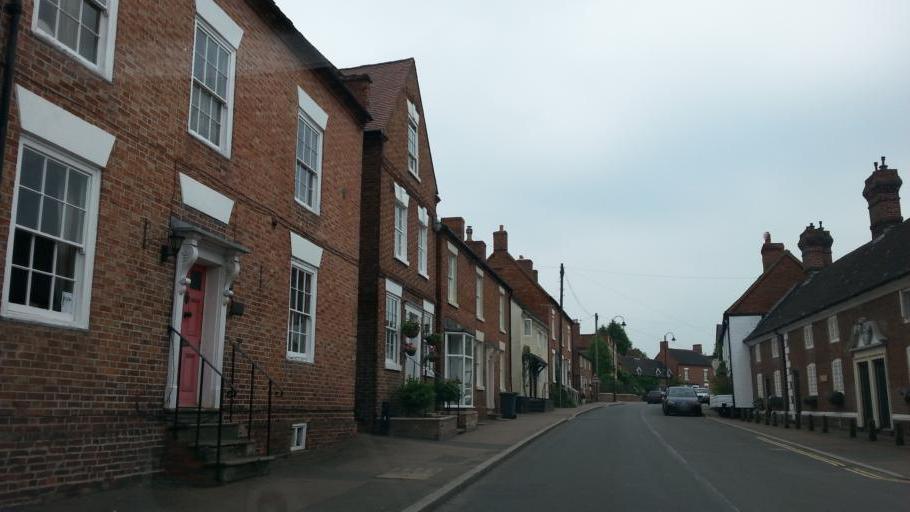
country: GB
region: England
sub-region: Staffordshire
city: Armitage
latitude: 52.8193
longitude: -1.8836
